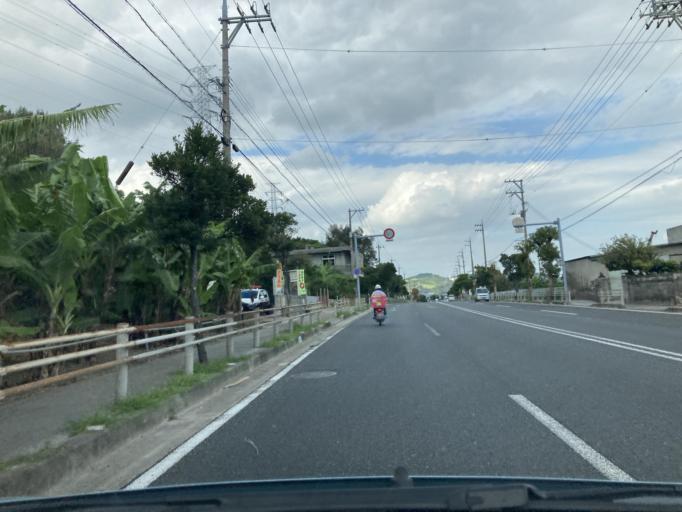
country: JP
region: Okinawa
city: Ginowan
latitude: 26.2501
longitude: 127.7826
